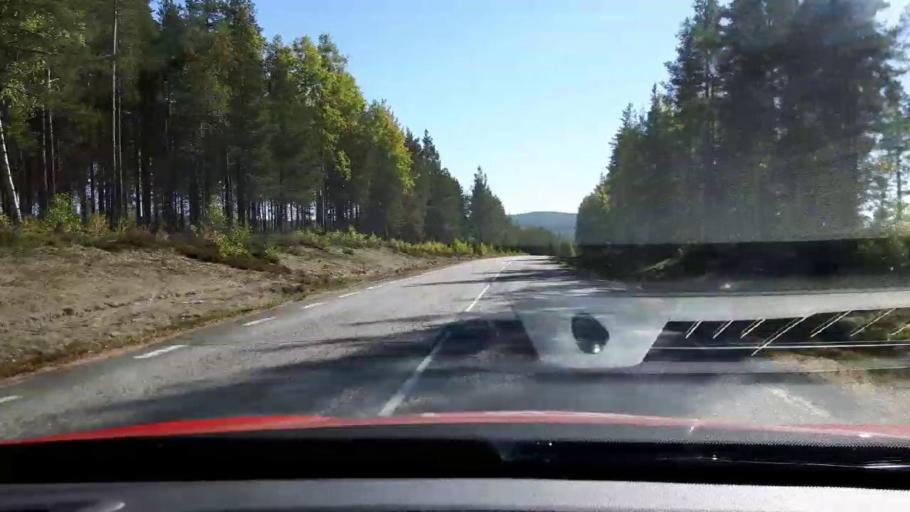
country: SE
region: Jaemtland
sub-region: Harjedalens Kommun
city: Sveg
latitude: 62.2978
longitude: 14.0721
